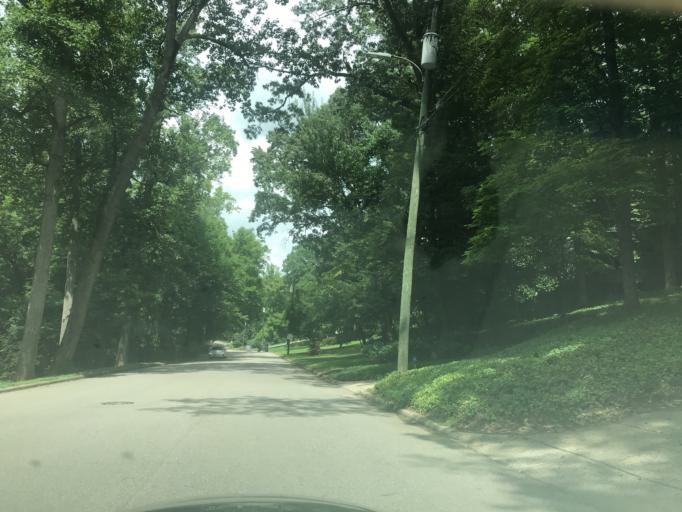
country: US
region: North Carolina
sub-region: Wake County
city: West Raleigh
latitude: 35.8129
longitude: -78.6390
